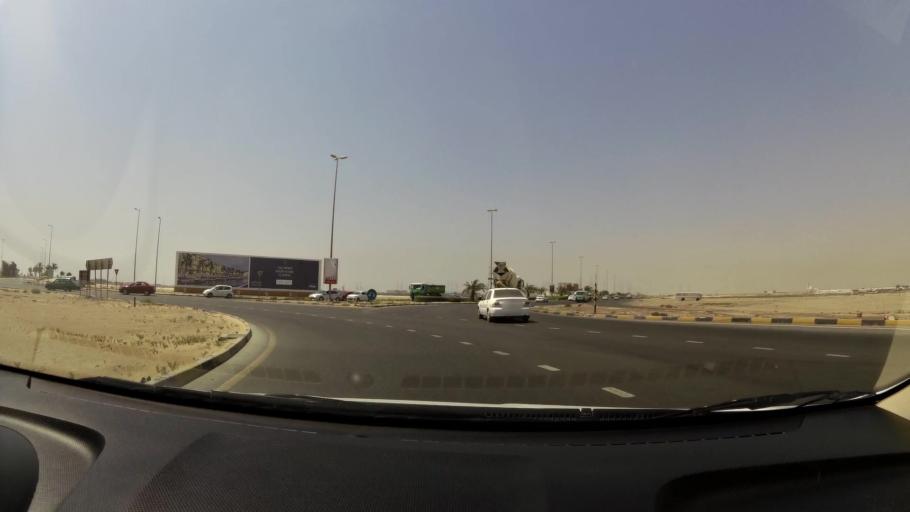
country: AE
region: Ajman
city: Ajman
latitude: 25.4345
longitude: 55.5045
